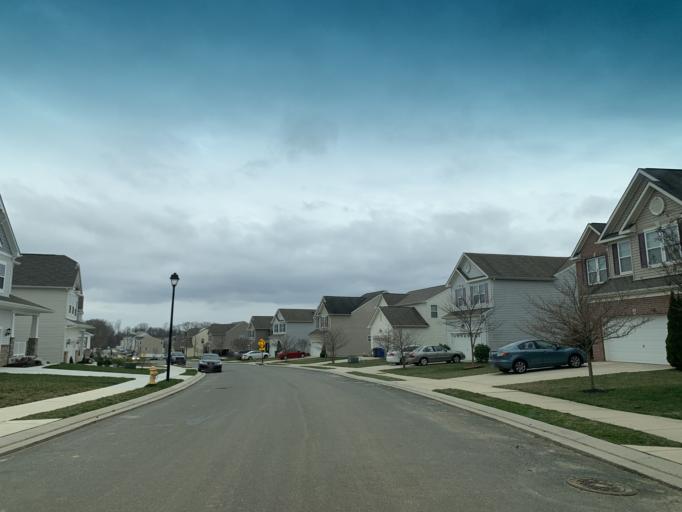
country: US
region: Maryland
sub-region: Harford County
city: Perryman
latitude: 39.4964
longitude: -76.2069
